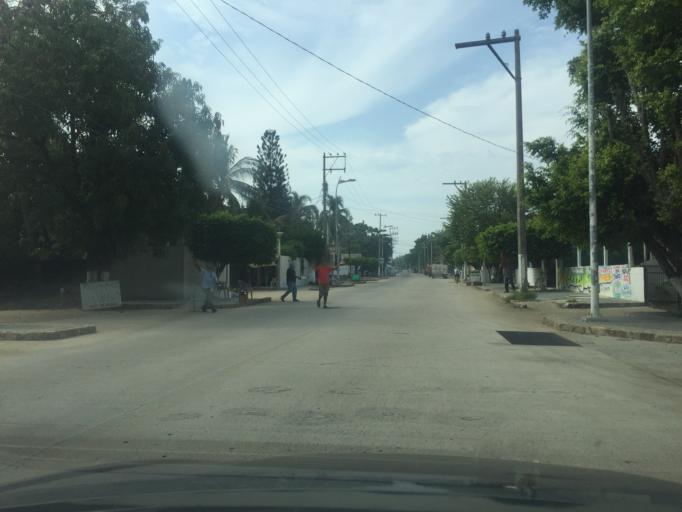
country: MX
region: Guerrero
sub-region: Coyuca de Benitez
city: Colonia Luces en el Mar
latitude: 16.8970
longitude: -99.9623
